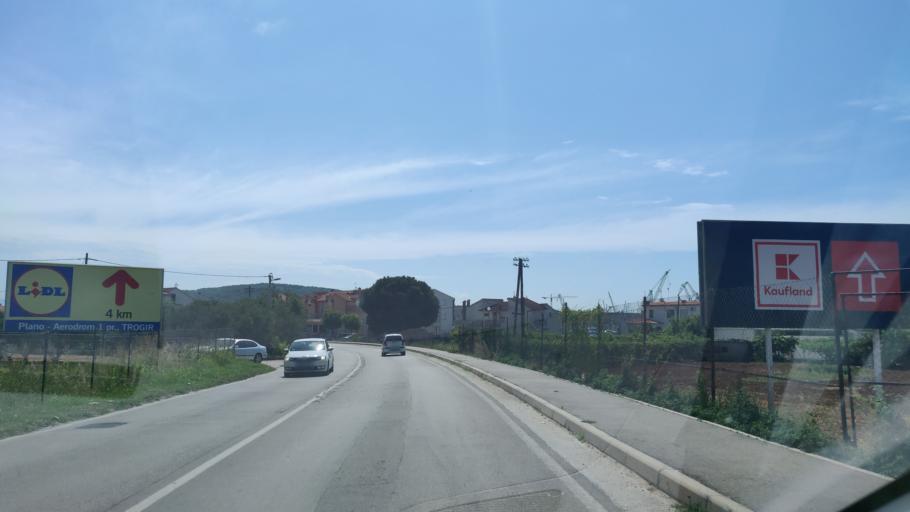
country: HR
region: Splitsko-Dalmatinska
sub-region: Grad Trogir
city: Trogir
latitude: 43.5180
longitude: 16.2373
